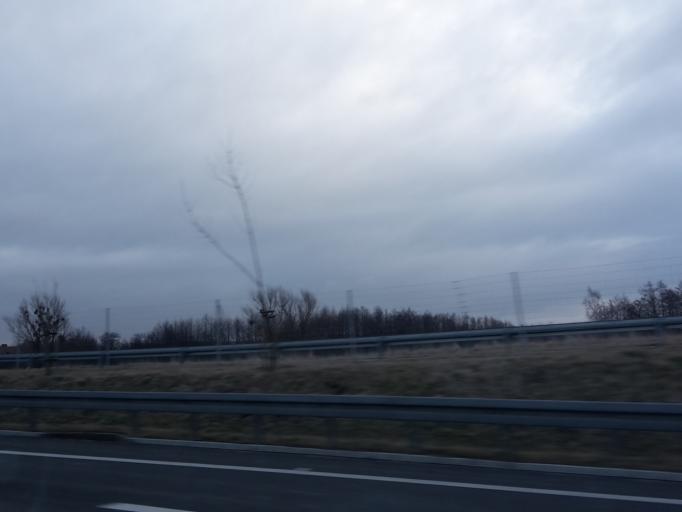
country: PL
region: Warmian-Masurian Voivodeship
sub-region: Powiat ostrodzki
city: Maldyty
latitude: 53.9750
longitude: 19.6972
